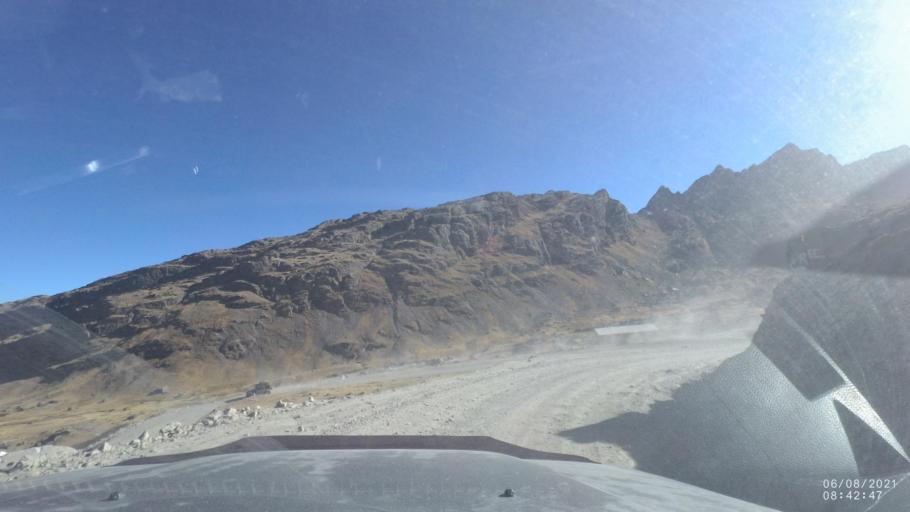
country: BO
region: Cochabamba
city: Sipe Sipe
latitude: -17.1679
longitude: -66.4106
